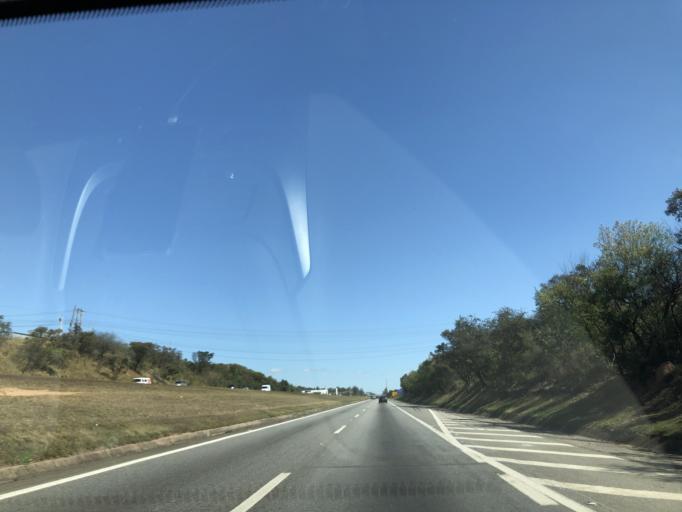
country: BR
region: Sao Paulo
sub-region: Sorocaba
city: Sorocaba
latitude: -23.4283
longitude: -47.3637
